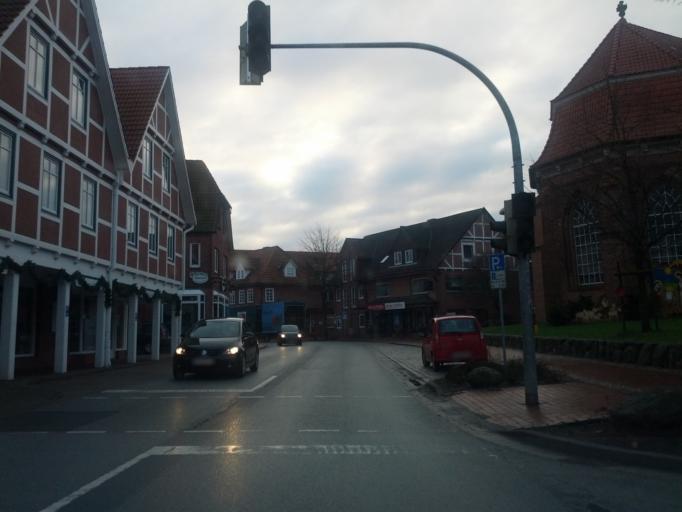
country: DE
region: Lower Saxony
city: Steinkirchen
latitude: 53.5607
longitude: 9.6086
